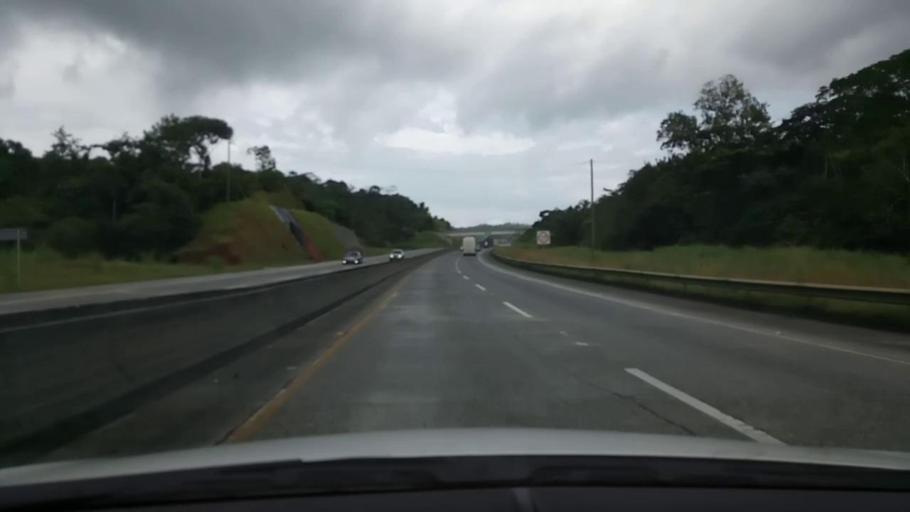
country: PA
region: Colon
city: Gatun
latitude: 9.2820
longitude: -79.7666
